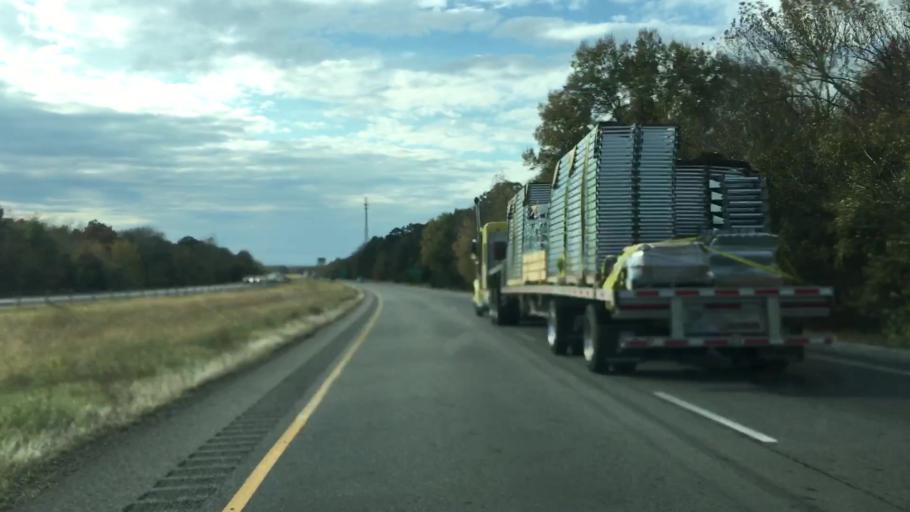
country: US
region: Arkansas
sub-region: Pope County
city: Pottsville
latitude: 35.2477
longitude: -93.0084
